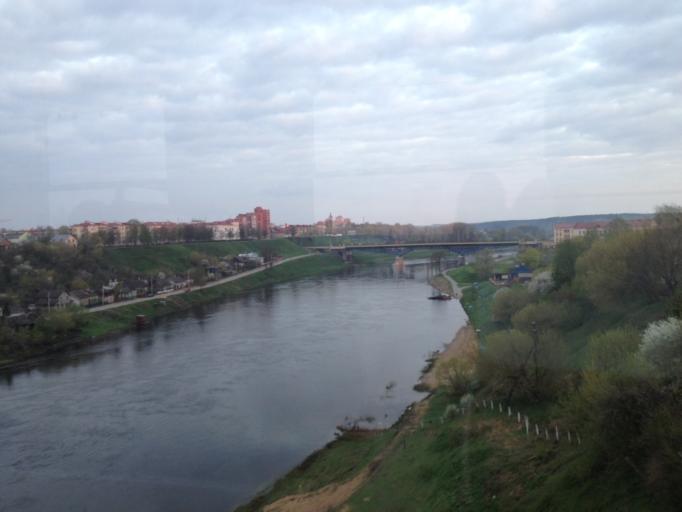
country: BY
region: Grodnenskaya
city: Hrodna
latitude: 53.6703
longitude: 23.8351
